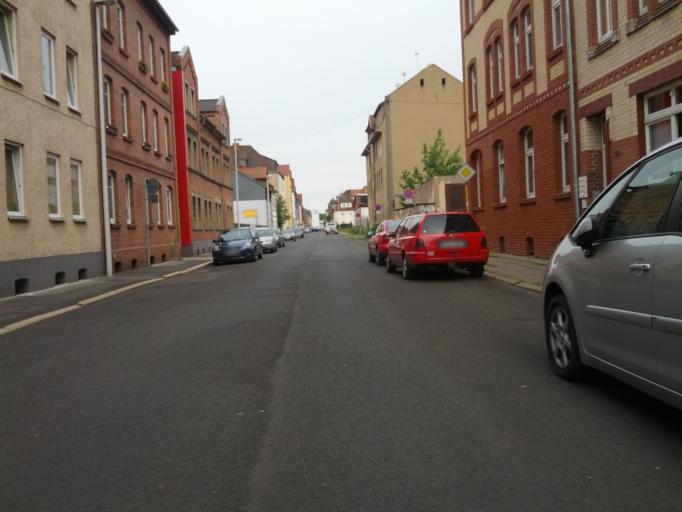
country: DE
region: Thuringia
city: Eisenach
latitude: 50.9805
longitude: 10.3091
